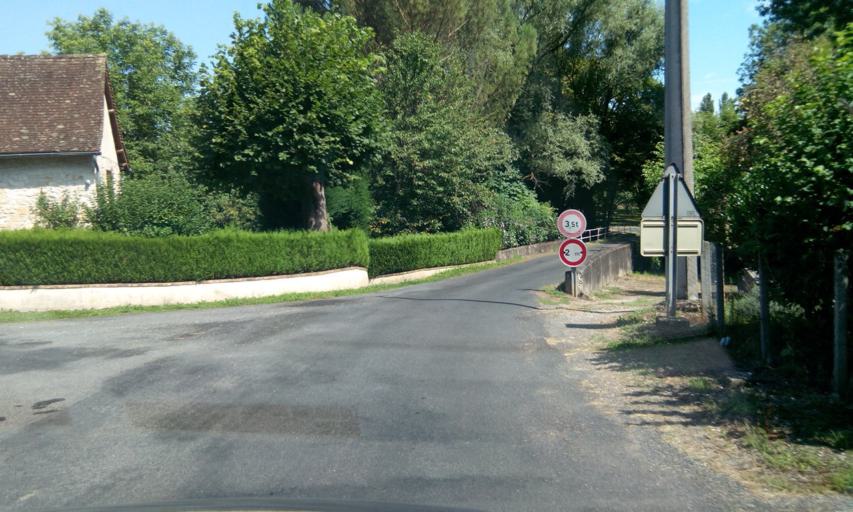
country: FR
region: Midi-Pyrenees
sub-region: Departement du Lot
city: Vayrac
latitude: 44.9395
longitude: 1.6619
